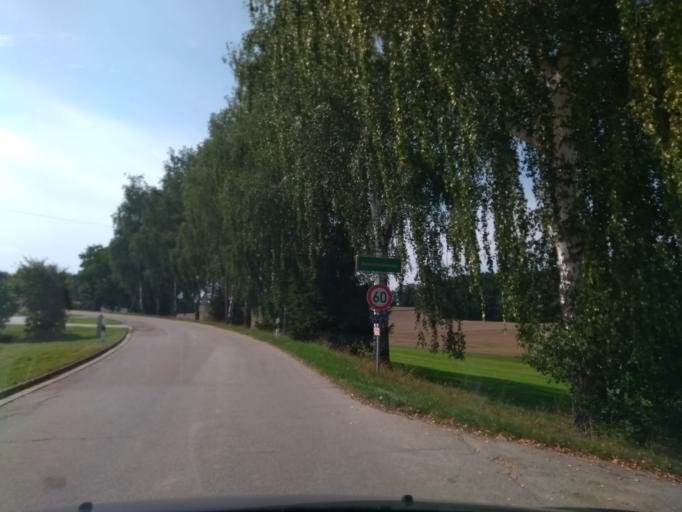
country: DE
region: Bavaria
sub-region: Upper Bavaria
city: Schwabhausen
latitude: 48.4018
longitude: 11.3593
